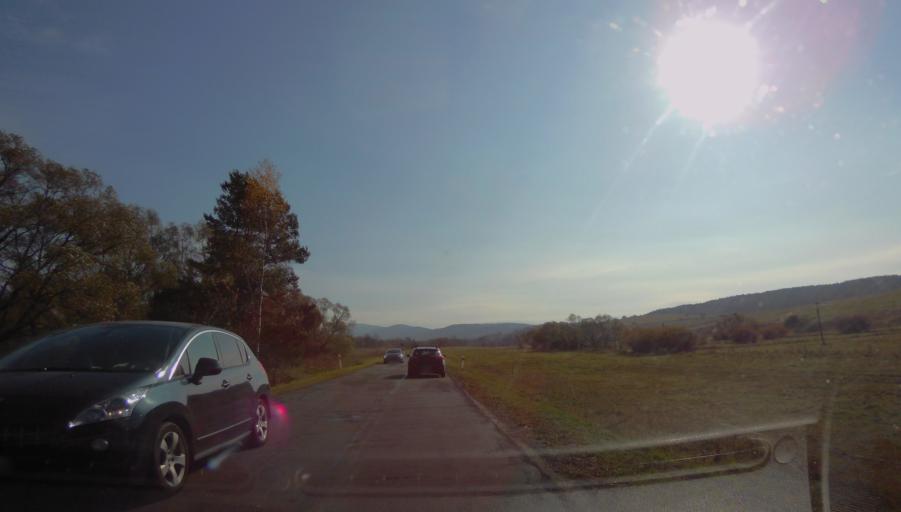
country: PL
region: Subcarpathian Voivodeship
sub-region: Powiat sanocki
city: Komancza
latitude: 49.2476
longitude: 22.1253
